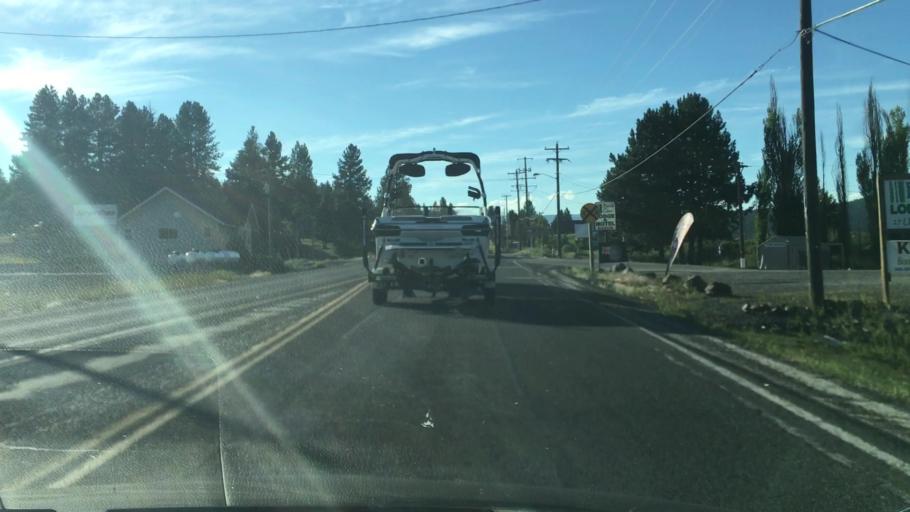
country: US
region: Idaho
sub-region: Valley County
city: Cascade
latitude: 44.5060
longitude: -116.0306
